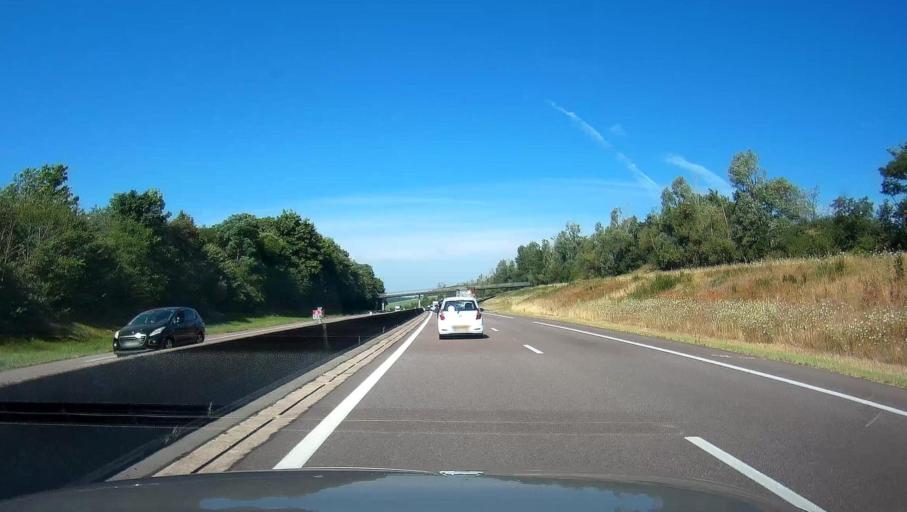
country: FR
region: Champagne-Ardenne
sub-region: Departement de la Haute-Marne
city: Nogent-le-Bas
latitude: 47.9584
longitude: 5.3991
